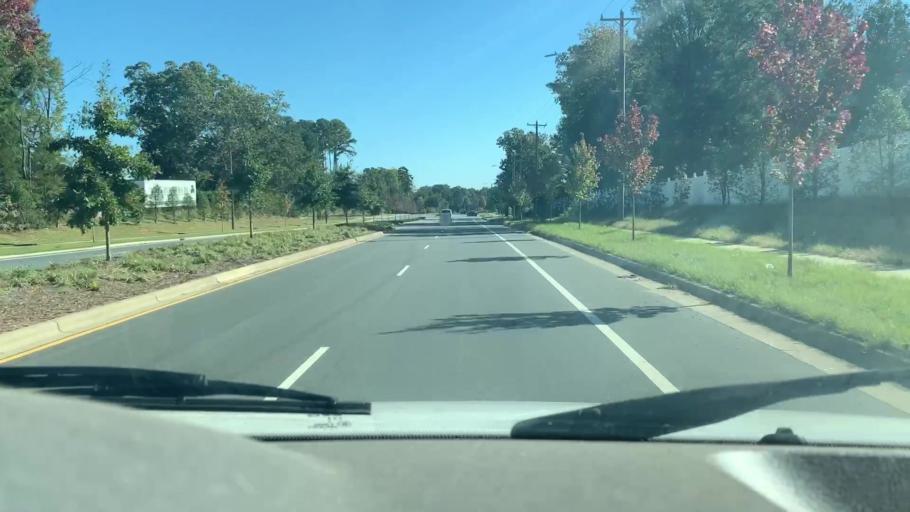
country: US
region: North Carolina
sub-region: Mecklenburg County
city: Charlotte
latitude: 35.2960
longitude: -80.7891
